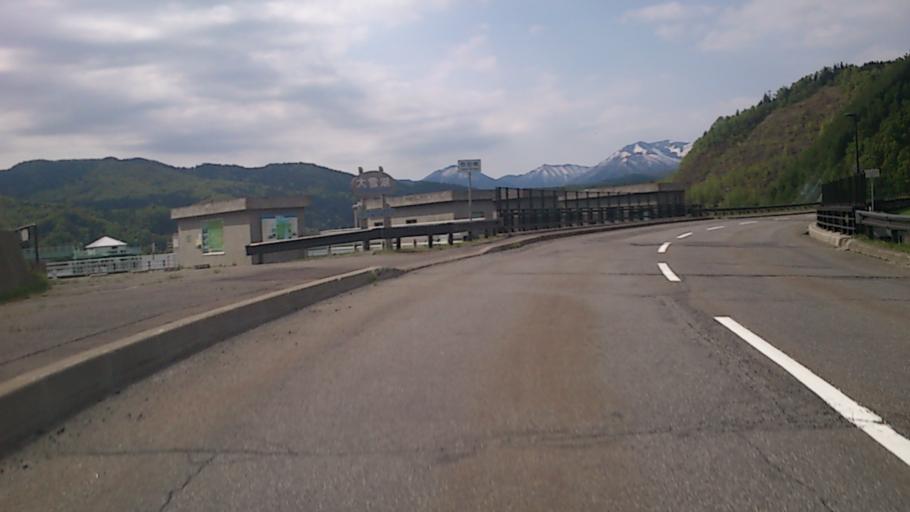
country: JP
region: Hokkaido
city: Kamikawa
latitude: 43.6784
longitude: 143.0375
